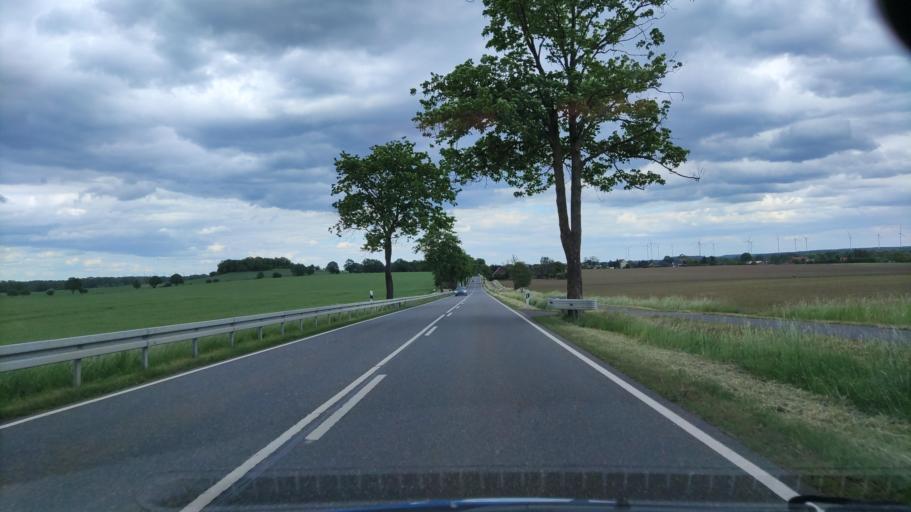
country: DE
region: Mecklenburg-Vorpommern
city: Lubz
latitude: 53.4661
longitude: 12.0928
